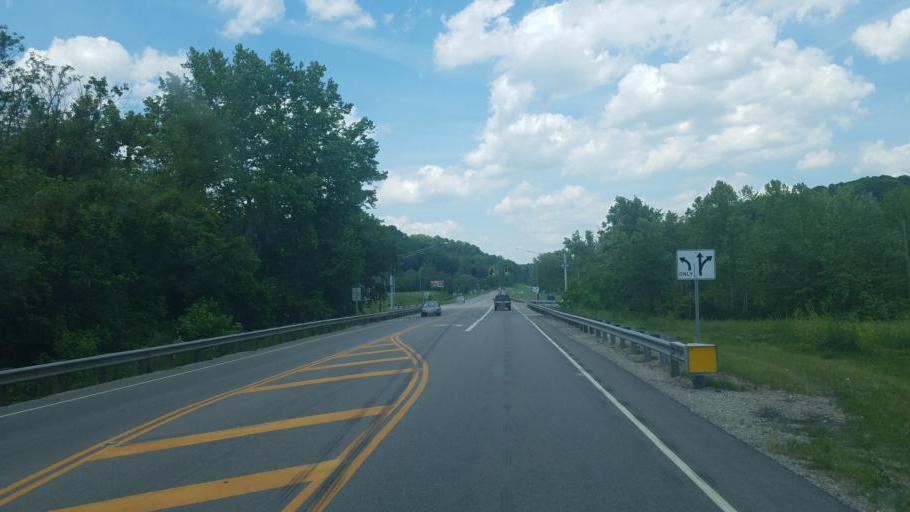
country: US
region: Ohio
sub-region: Meigs County
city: Middleport
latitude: 39.0229
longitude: -82.0667
